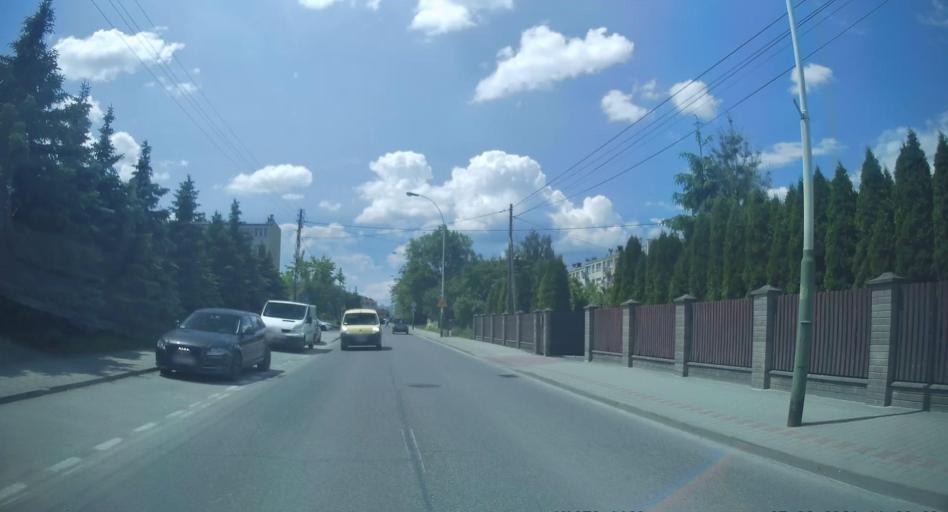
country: PL
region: Subcarpathian Voivodeship
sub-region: Powiat debicki
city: Debica
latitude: 50.0575
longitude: 21.4297
